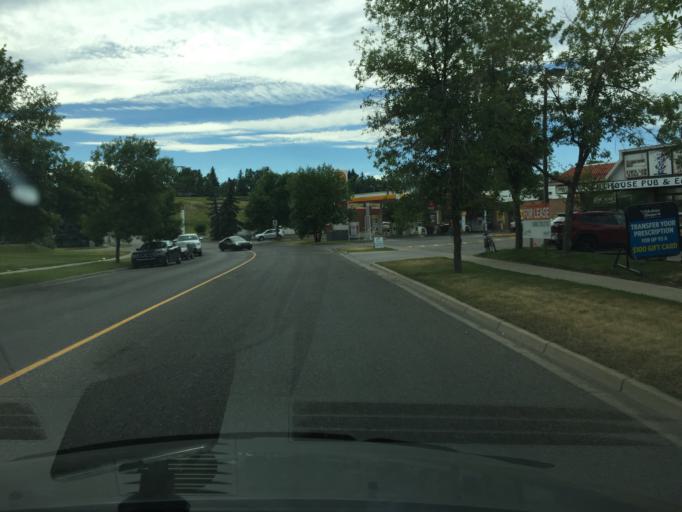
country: CA
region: Alberta
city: Calgary
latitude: 50.9279
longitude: -114.0276
